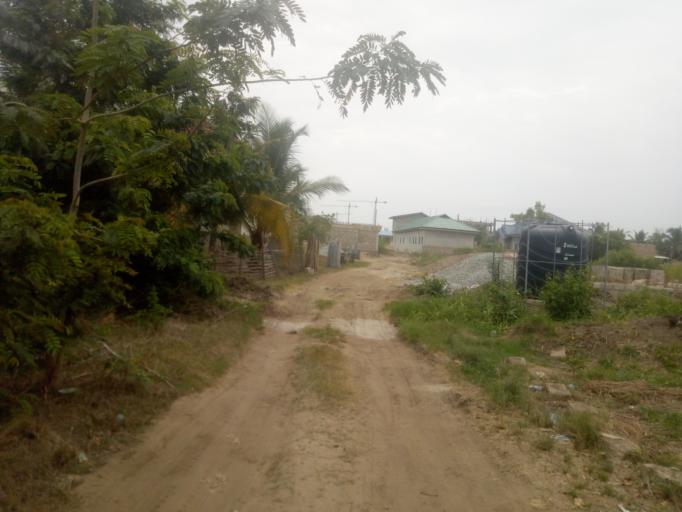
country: GH
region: Central
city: Winneba
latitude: 5.3765
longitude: -0.6311
